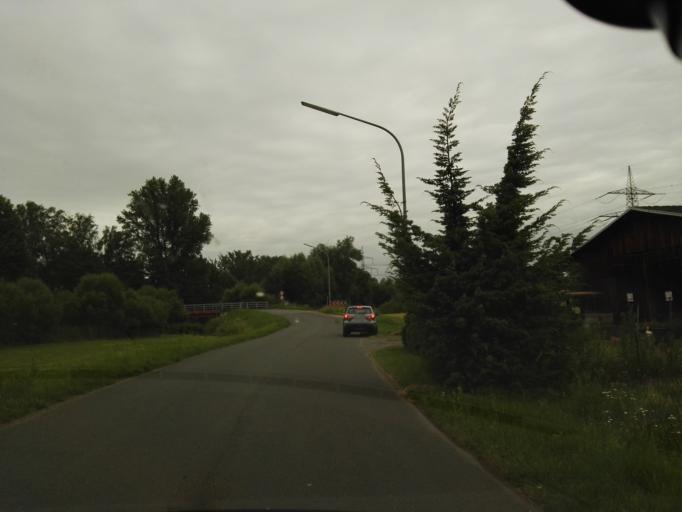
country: DE
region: Bavaria
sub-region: Upper Franconia
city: Redwitz an der Rodach
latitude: 50.1758
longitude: 11.2017
